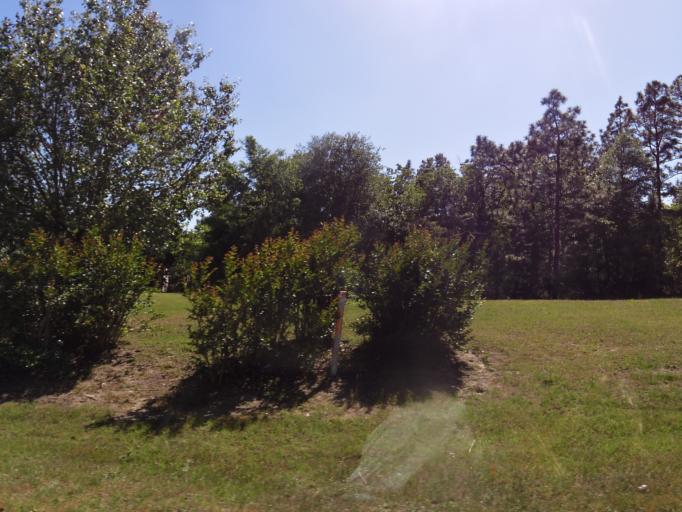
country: US
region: South Carolina
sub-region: Barnwell County
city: Williston
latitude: 33.4862
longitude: -81.5184
